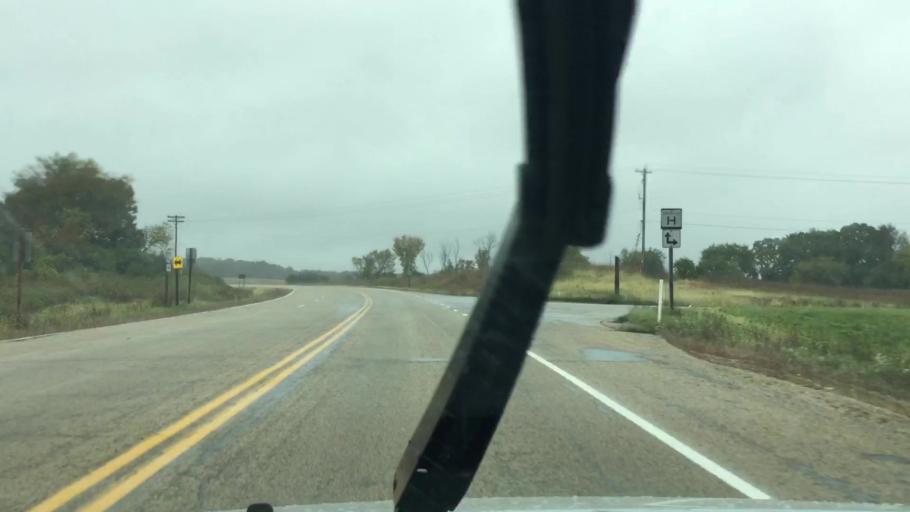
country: US
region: Wisconsin
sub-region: Jefferson County
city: Palmyra
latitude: 42.8844
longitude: -88.5600
